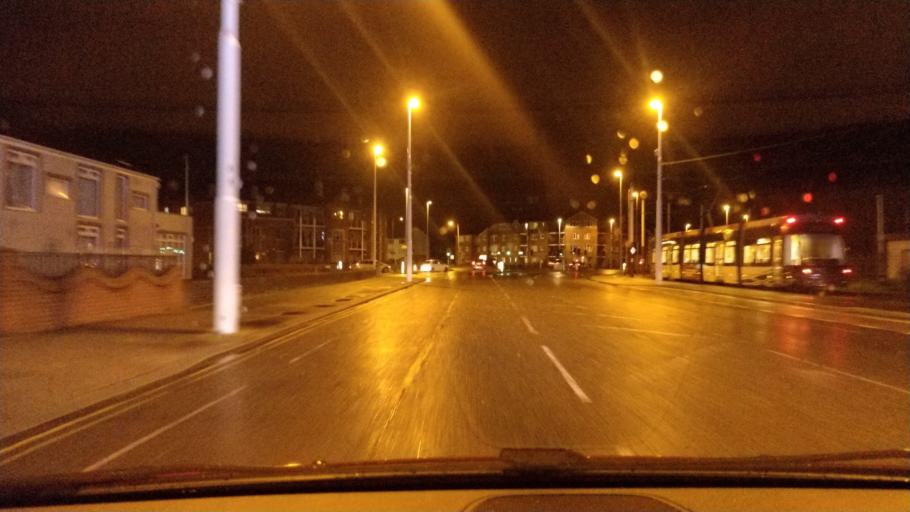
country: GB
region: England
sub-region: Blackpool
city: Blackpool
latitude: 53.7779
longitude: -3.0554
